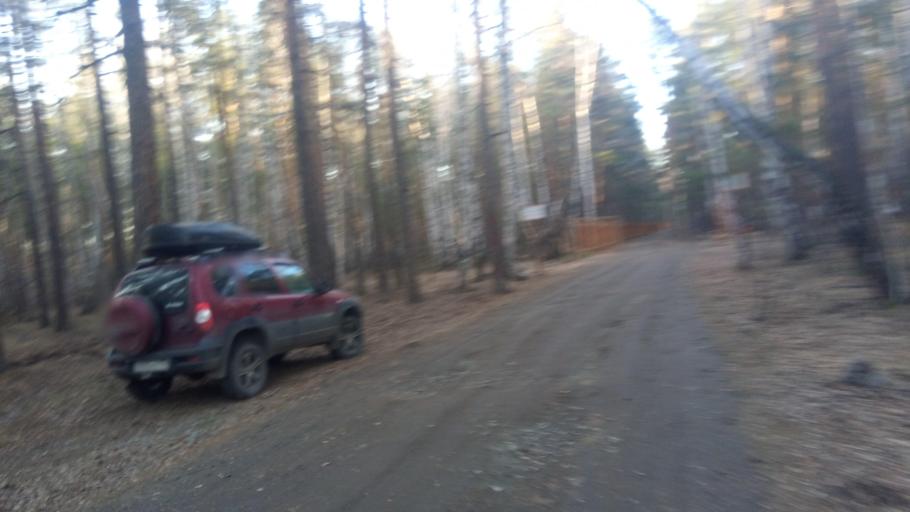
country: RU
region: Chelyabinsk
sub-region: Gorod Chelyabinsk
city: Chelyabinsk
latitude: 55.1251
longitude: 61.3461
